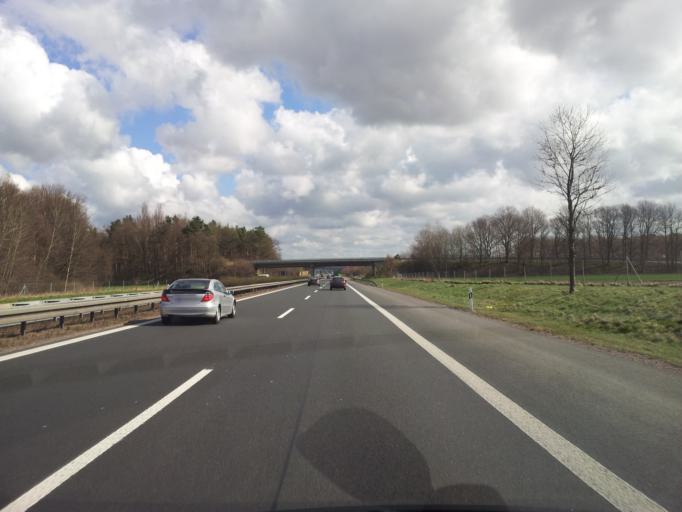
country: DE
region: Saxony
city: Ottendorf-Okrilla
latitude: 51.1601
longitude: 13.7914
